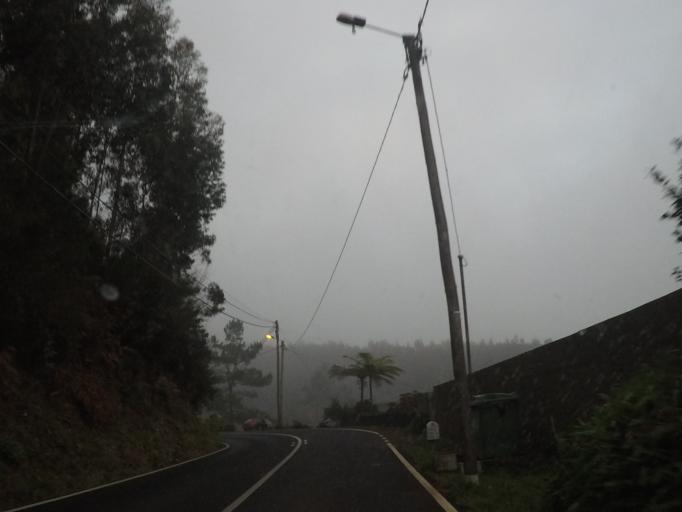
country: PT
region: Madeira
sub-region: Santa Cruz
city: Camacha
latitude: 32.7089
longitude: -16.8321
